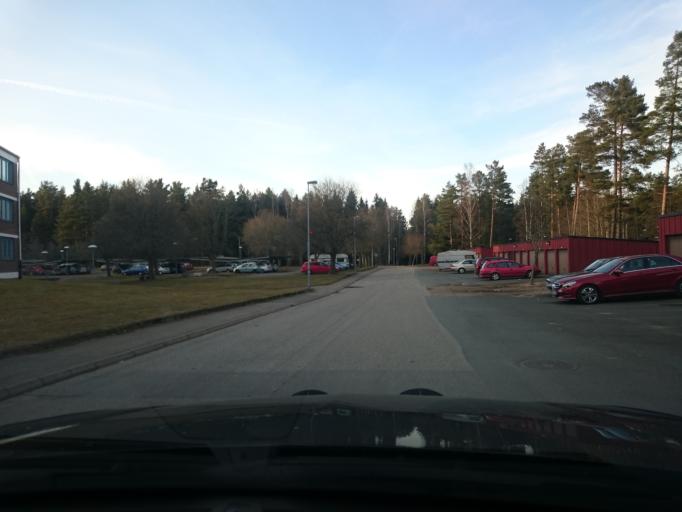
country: SE
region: Joenkoeping
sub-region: Vetlanda Kommun
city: Vetlanda
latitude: 57.4176
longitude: 15.0971
